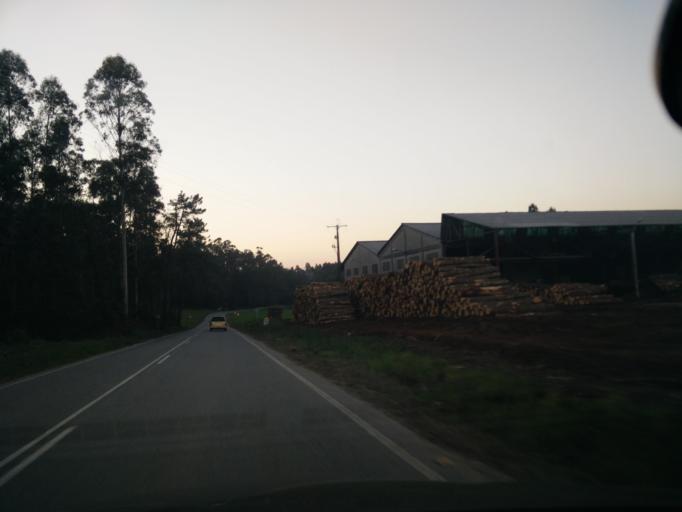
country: ES
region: Galicia
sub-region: Provincia da Coruna
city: Monfero
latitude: 43.3736
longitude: -8.0729
